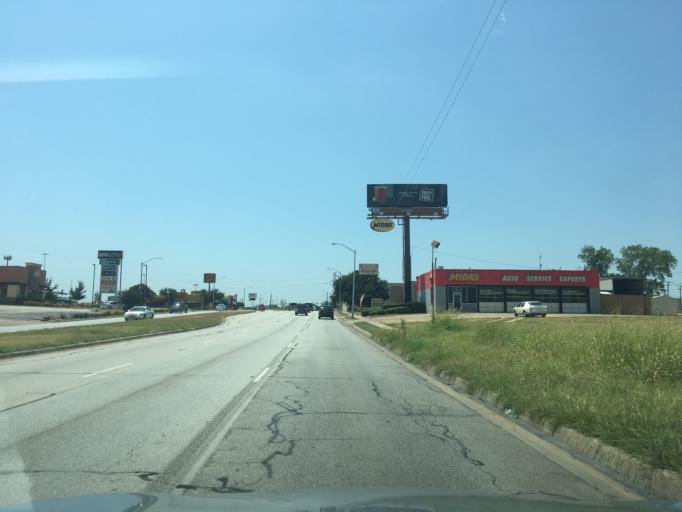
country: US
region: Texas
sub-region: Tarrant County
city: Edgecliff Village
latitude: 32.6528
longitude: -97.3646
